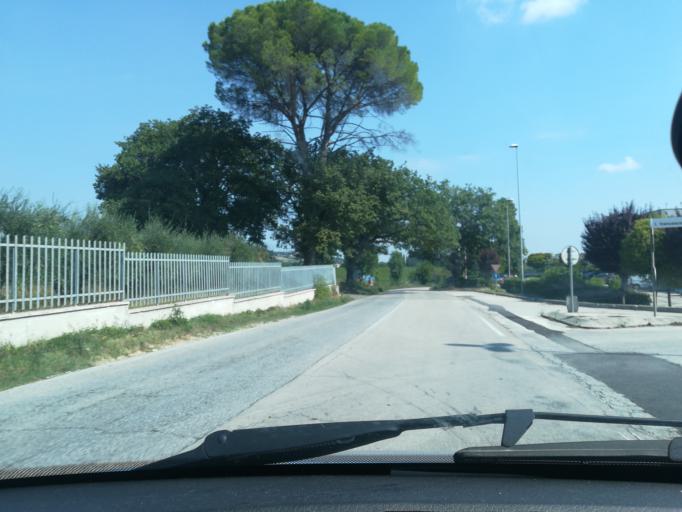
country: IT
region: The Marches
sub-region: Provincia di Macerata
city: Pollenza
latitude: 43.2237
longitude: 13.3349
